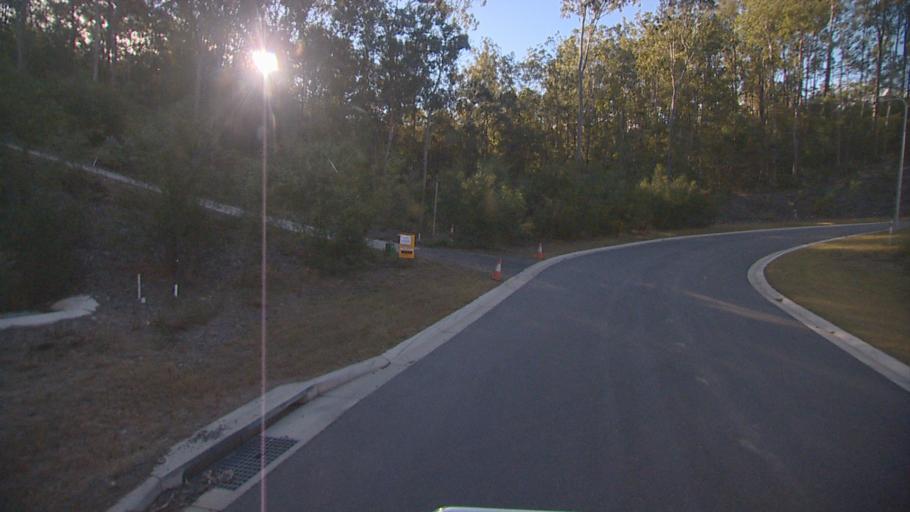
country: AU
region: Queensland
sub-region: Logan
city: Cedar Vale
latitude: -27.9279
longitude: 153.0509
